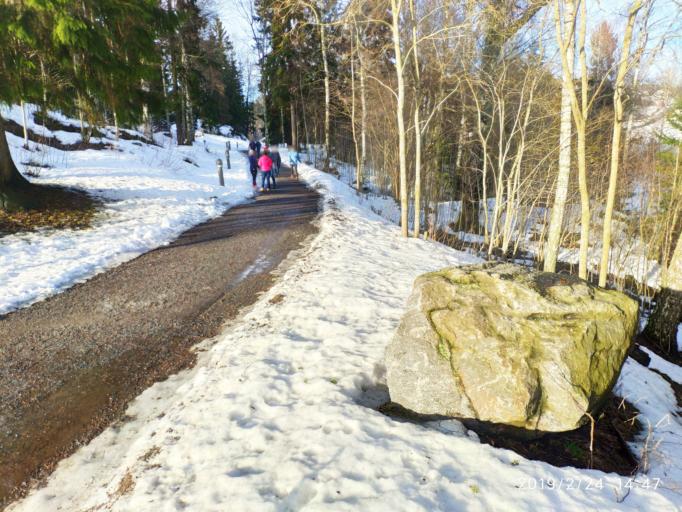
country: NO
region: Akershus
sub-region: Lorenskog
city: Kjenn
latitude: 59.9316
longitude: 10.9623
